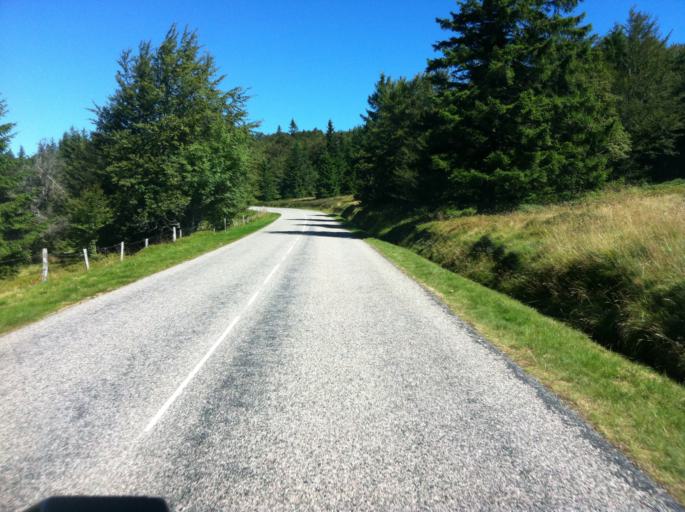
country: FR
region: Alsace
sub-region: Departement du Haut-Rhin
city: Soultzeren
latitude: 48.0857
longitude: 7.0471
